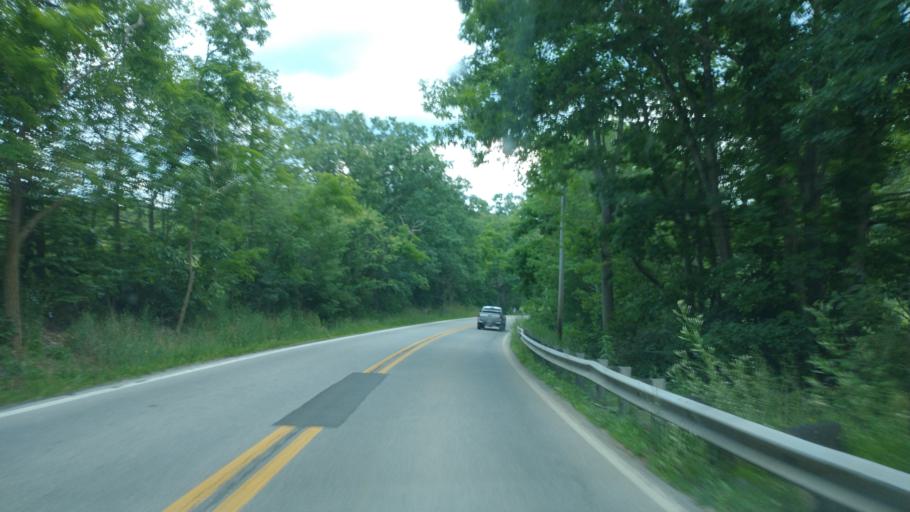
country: US
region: West Virginia
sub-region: Mercer County
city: Athens
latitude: 37.4464
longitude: -81.0014
